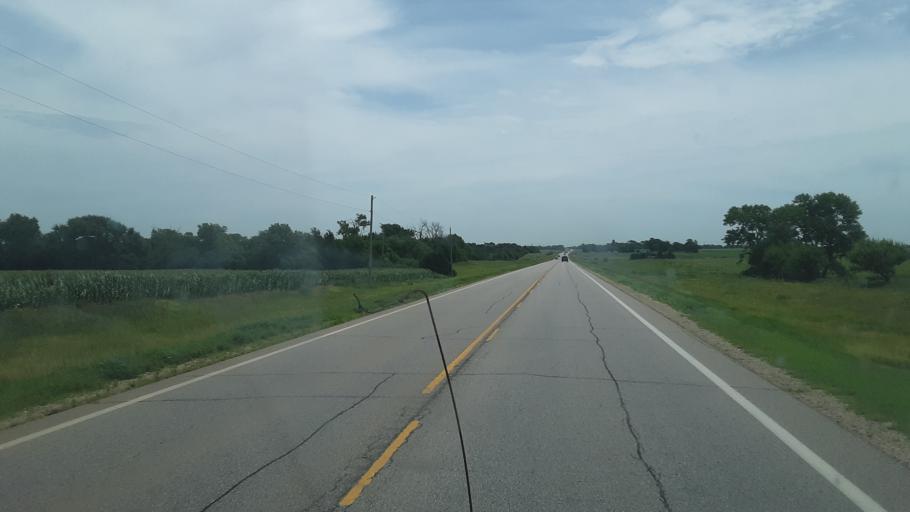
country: US
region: Kansas
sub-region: Butler County
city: El Dorado
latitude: 37.8106
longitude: -96.7094
